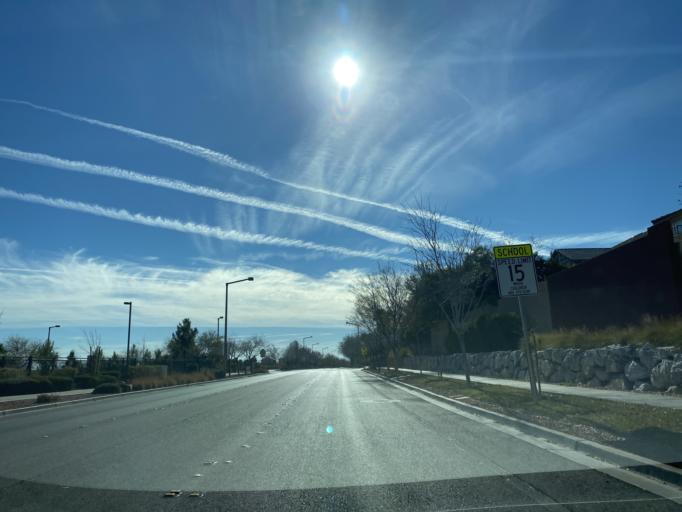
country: US
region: Nevada
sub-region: Clark County
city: Summerlin South
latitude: 36.1533
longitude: -115.3186
